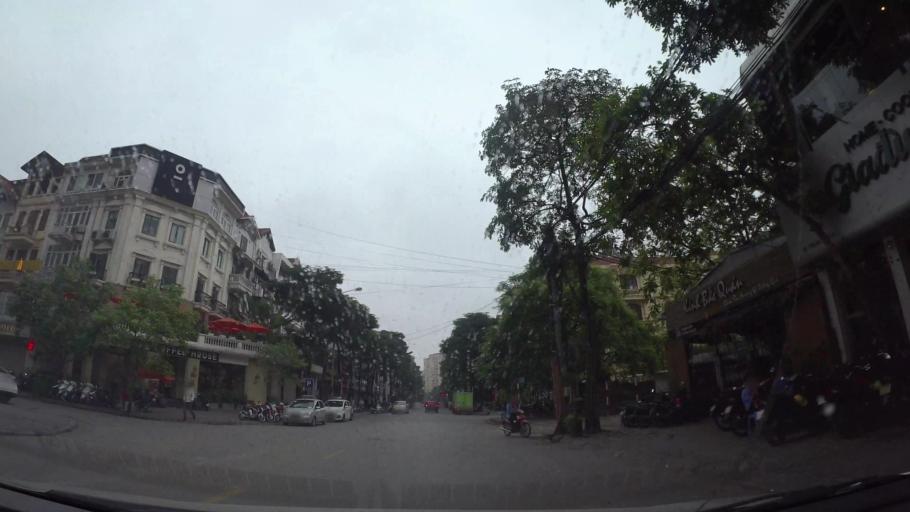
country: VN
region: Ha Noi
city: Cau Giay
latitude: 21.0144
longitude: 105.8020
